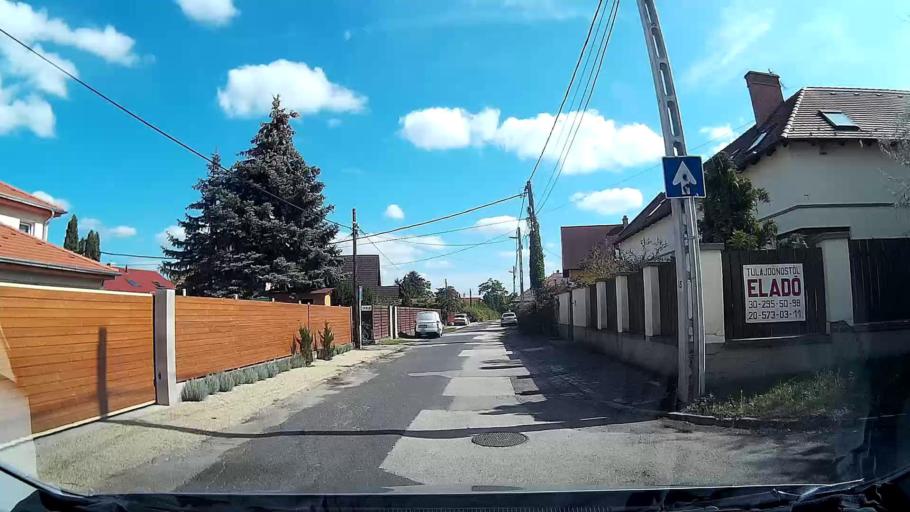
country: HU
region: Pest
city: Szentendre
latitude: 47.6759
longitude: 19.0747
